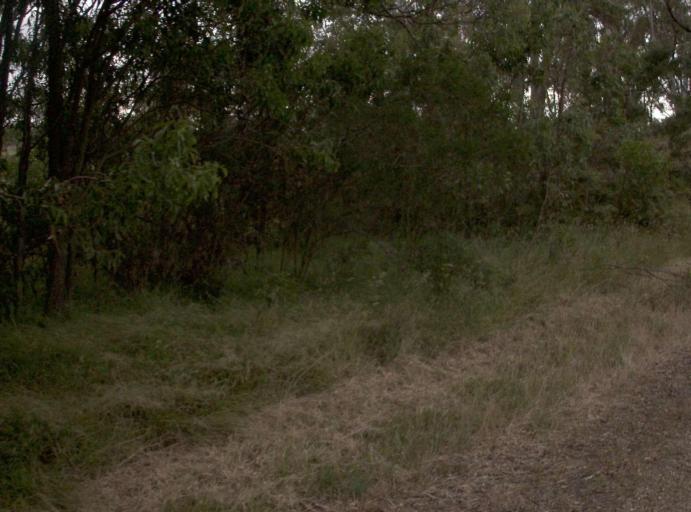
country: AU
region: Victoria
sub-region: Wellington
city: Sale
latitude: -38.0038
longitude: 147.2918
